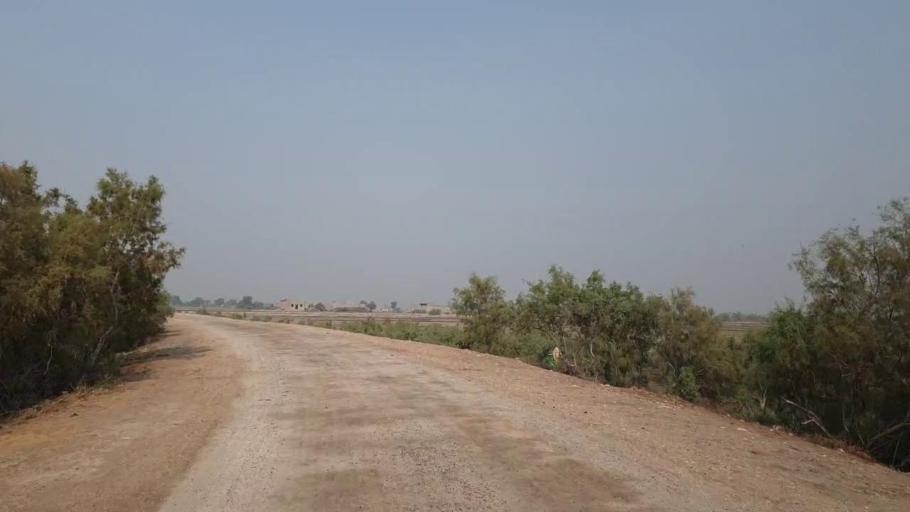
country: PK
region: Sindh
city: Bhan
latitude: 26.4905
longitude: 67.7007
